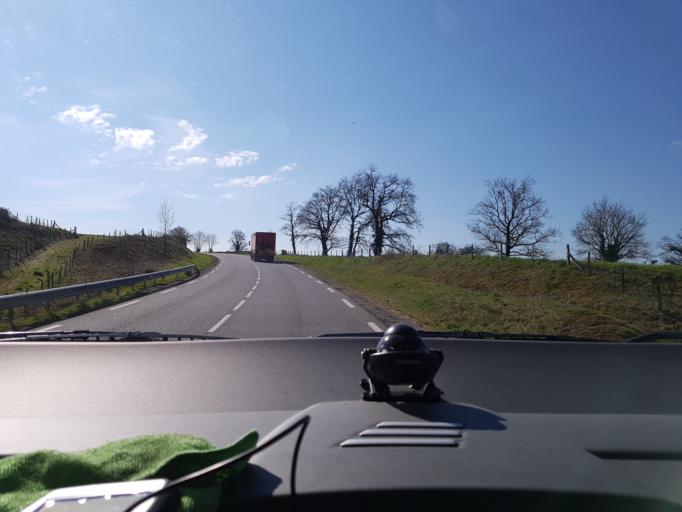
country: FR
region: Midi-Pyrenees
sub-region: Departement de l'Aveyron
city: Moyrazes
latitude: 44.3748
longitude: 2.4595
